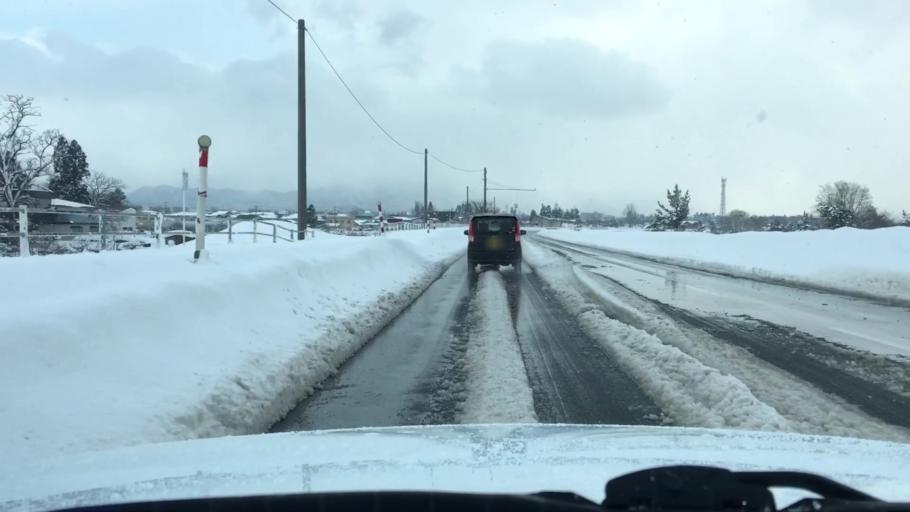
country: JP
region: Aomori
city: Hirosaki
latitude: 40.6272
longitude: 140.4742
